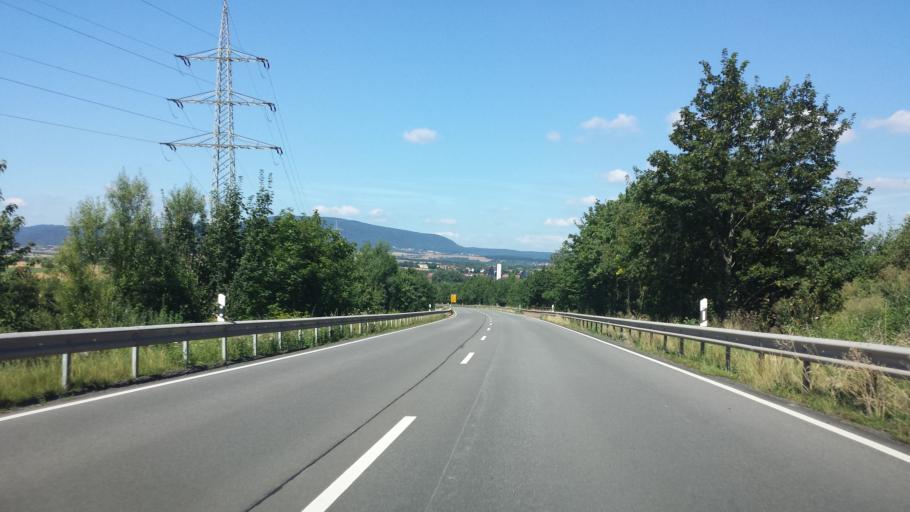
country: DE
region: Rheinland-Pfalz
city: Gollheim
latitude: 49.5927
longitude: 8.0361
